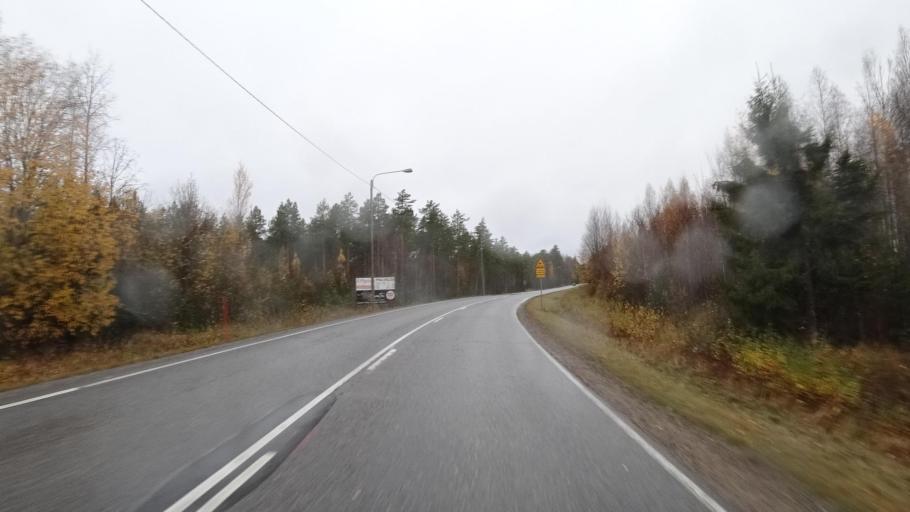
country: FI
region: Northern Savo
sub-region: Koillis-Savo
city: Tuusniemi
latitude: 62.7945
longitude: 28.5248
